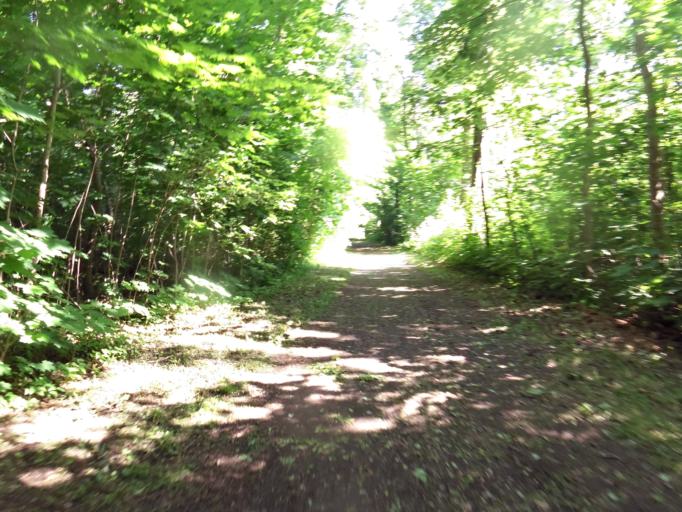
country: DE
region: Saxony
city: Leipzig
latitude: 51.3519
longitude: 12.3540
